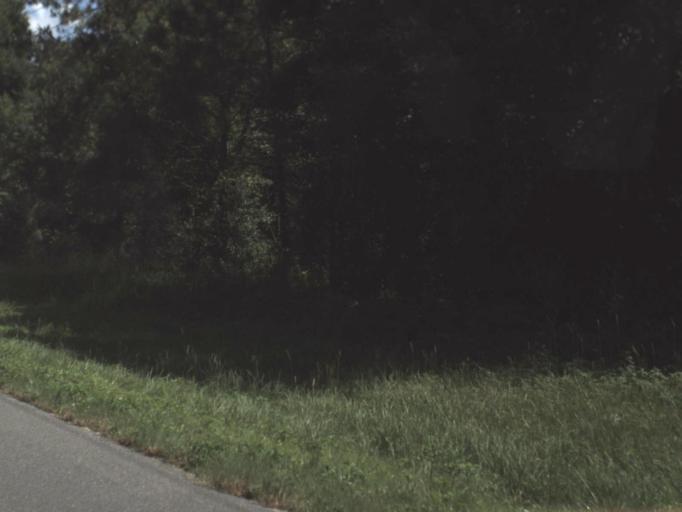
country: US
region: Florida
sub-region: Clay County
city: Keystone Heights
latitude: 29.7360
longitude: -81.9599
